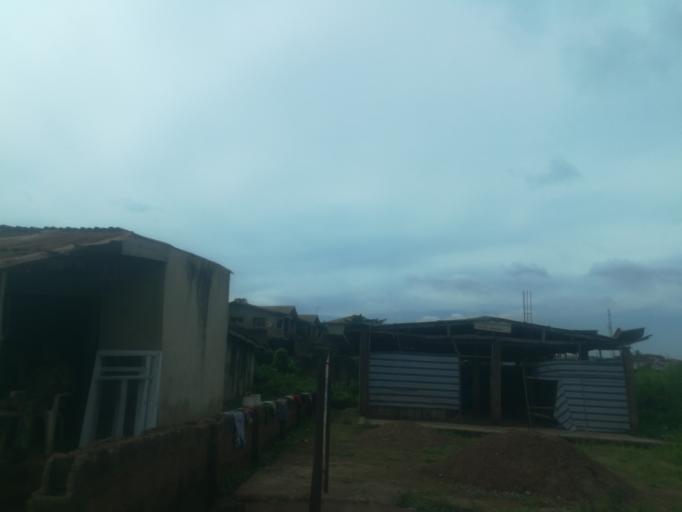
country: NG
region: Oyo
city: Ibadan
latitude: 7.3781
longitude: 3.9623
